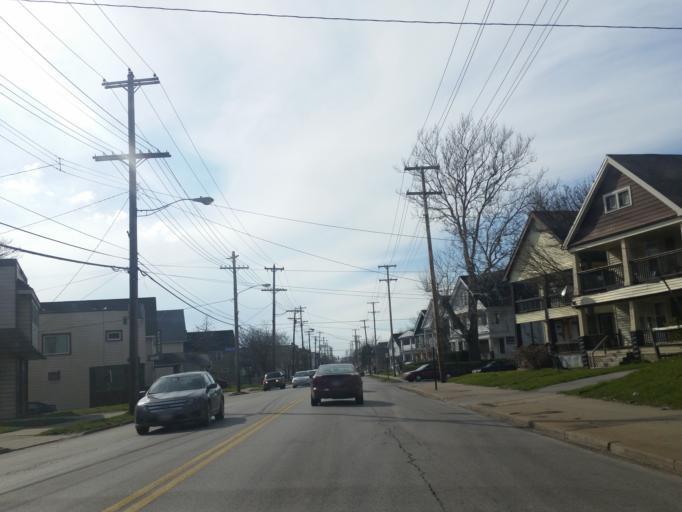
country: US
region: Ohio
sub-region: Cuyahoga County
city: Brooklyn
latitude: 41.4635
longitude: -81.7419
